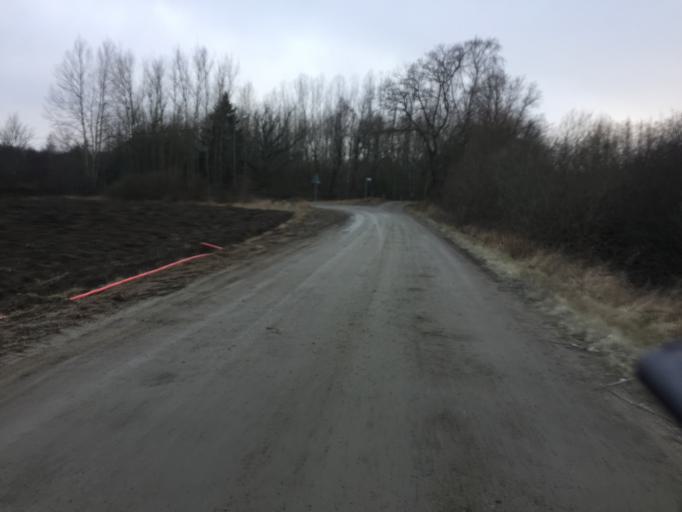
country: SE
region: Blekinge
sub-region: Karlshamns Kommun
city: Morrum
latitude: 56.1763
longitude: 14.7723
